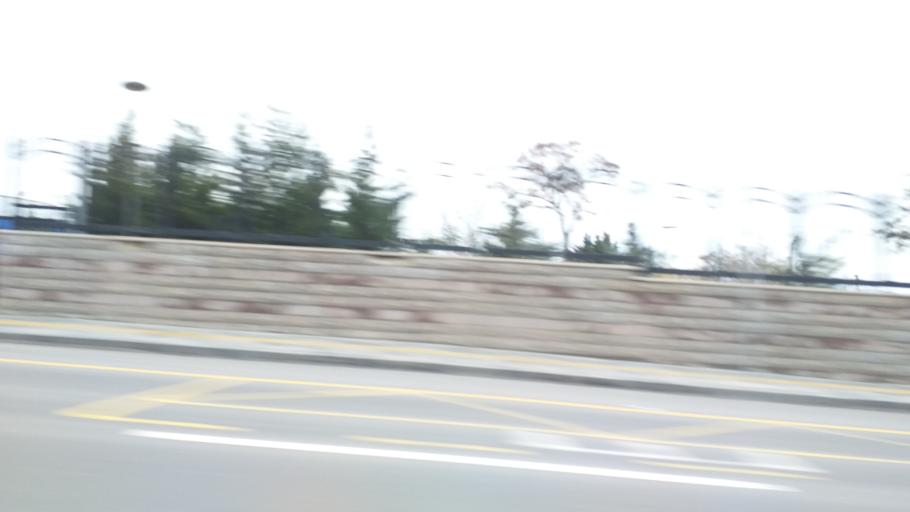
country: TR
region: Ankara
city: Ankara
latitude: 39.9296
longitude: 32.8136
